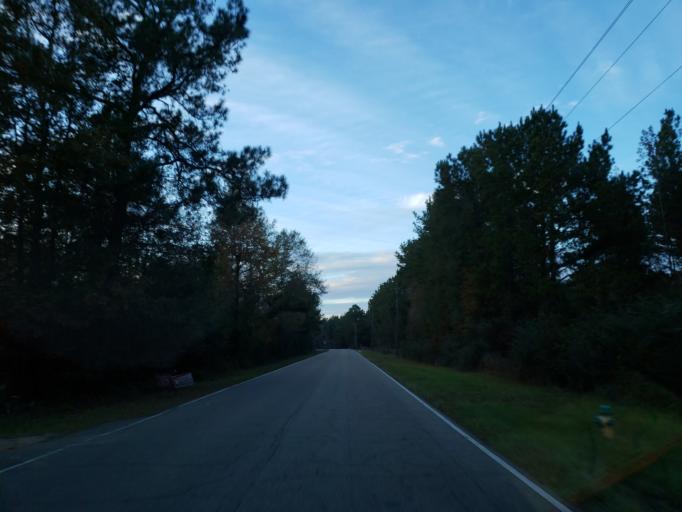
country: US
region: Mississippi
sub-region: Forrest County
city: Hattiesburg
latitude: 31.2770
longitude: -89.2467
